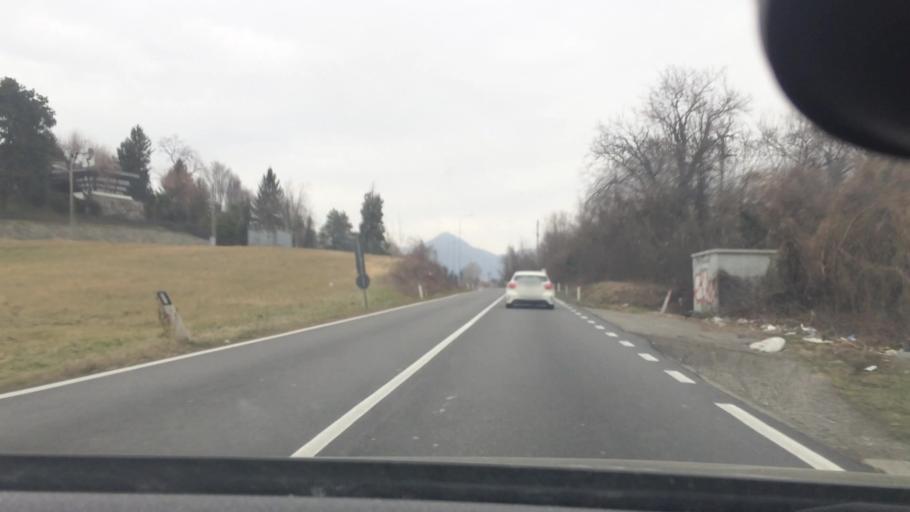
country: IT
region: Lombardy
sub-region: Provincia di Como
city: Nobile-Monguzzo
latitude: 45.7701
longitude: 9.2299
